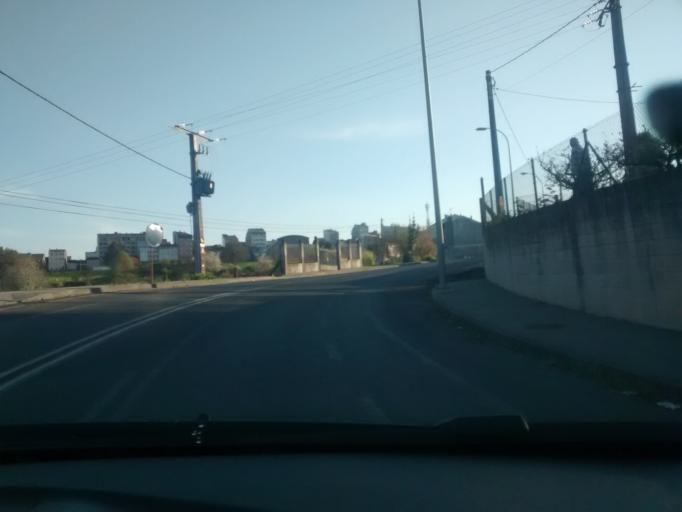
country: ES
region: Galicia
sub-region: Provincia de Pontevedra
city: A Estrada
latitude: 42.6941
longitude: -8.4834
